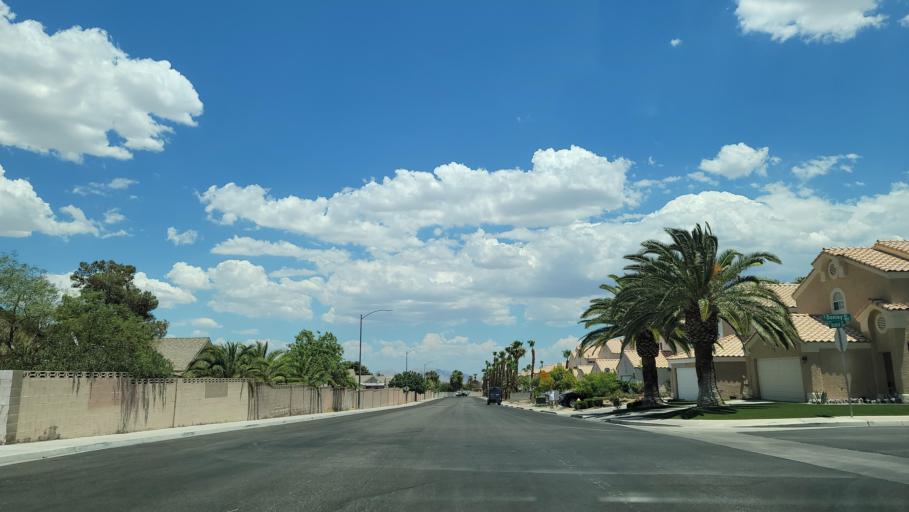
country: US
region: Nevada
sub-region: Clark County
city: Spring Valley
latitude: 36.1628
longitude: -115.2726
